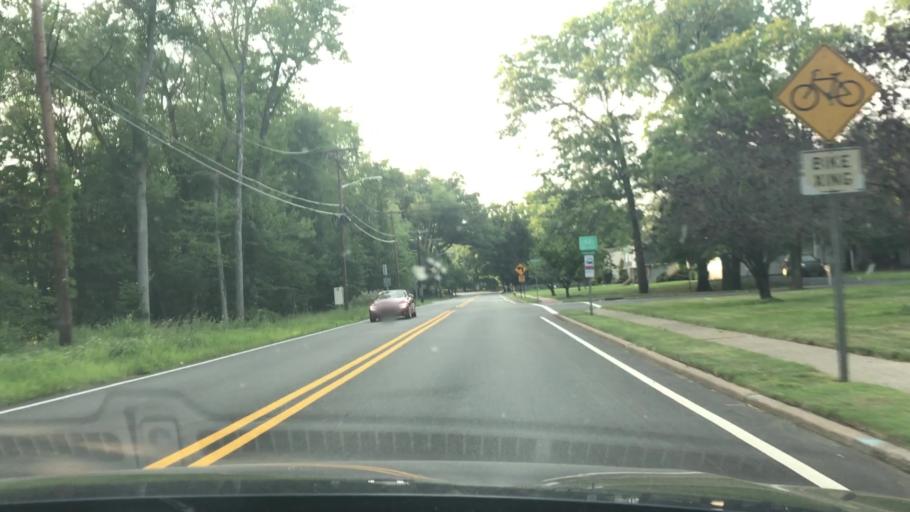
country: US
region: New Jersey
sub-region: Bergen County
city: Harrington Park
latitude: 40.9885
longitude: -73.9964
